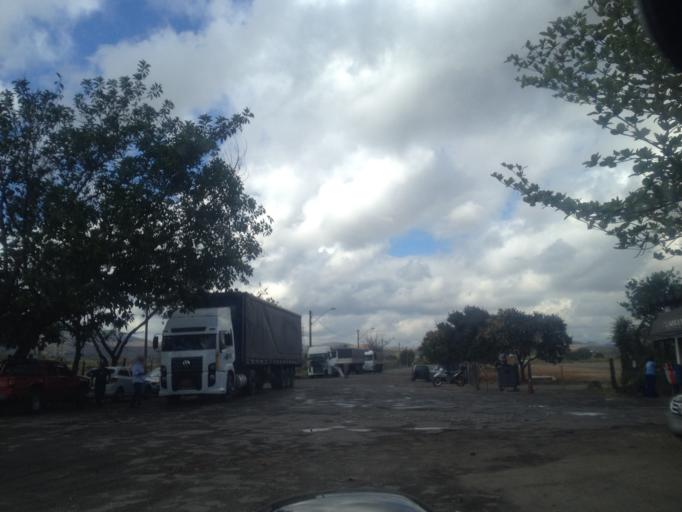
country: BR
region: Rio de Janeiro
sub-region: Resende
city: Resende
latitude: -22.4478
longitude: -44.3745
